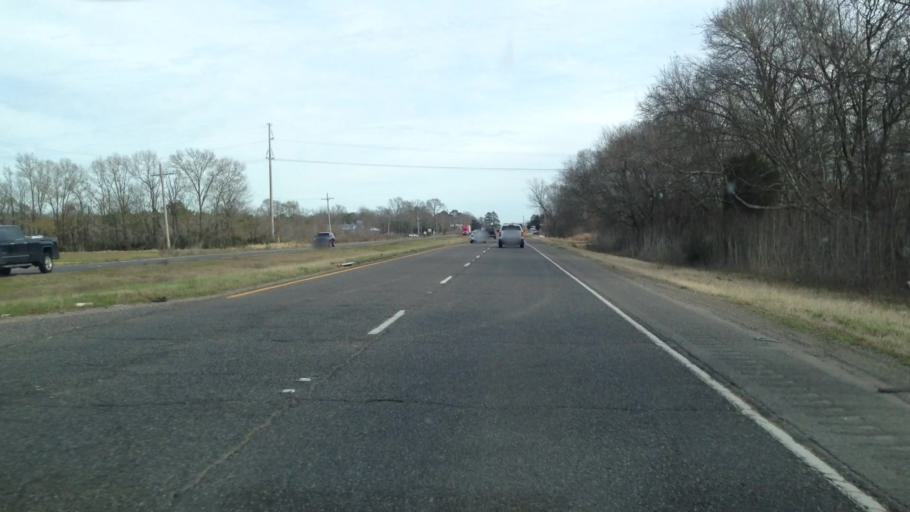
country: US
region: Louisiana
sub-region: Saint Landry Parish
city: Port Barre
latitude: 30.5473
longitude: -91.9788
